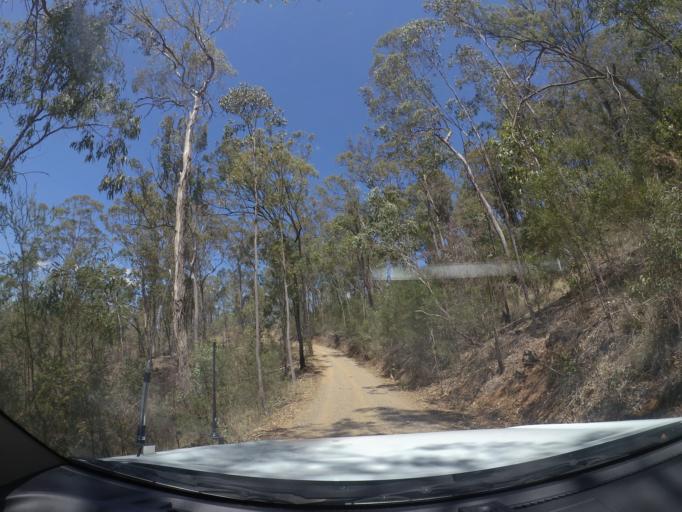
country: AU
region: Queensland
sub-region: Ipswich
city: Deebing Heights
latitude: -27.8314
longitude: 152.8266
